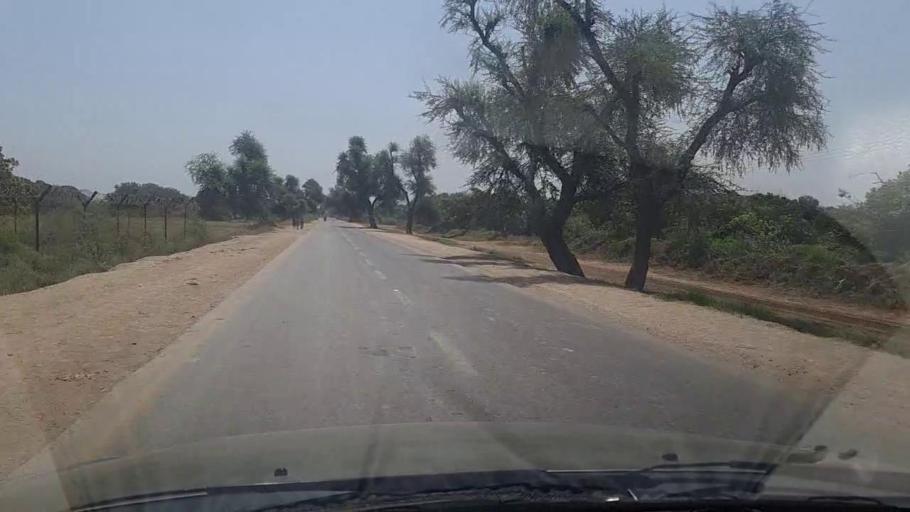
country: PK
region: Sindh
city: Tando Jam
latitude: 25.3325
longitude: 68.5374
